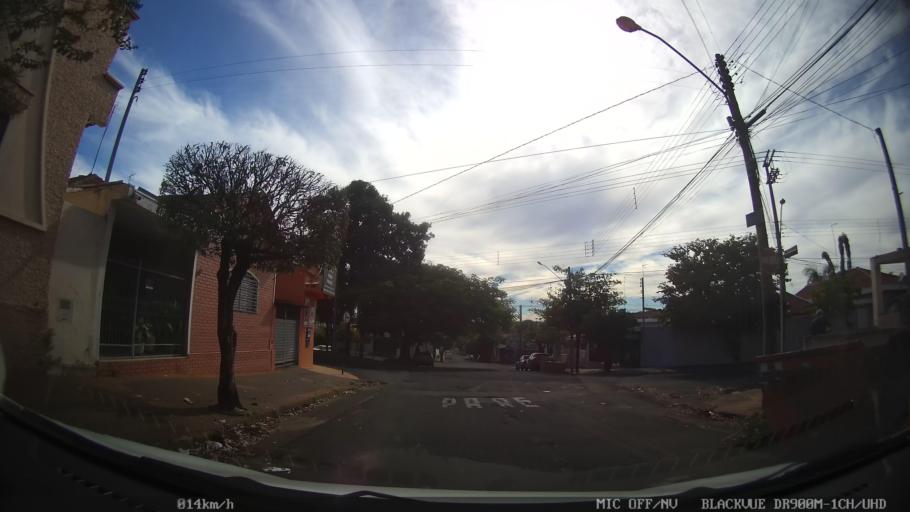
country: BR
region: Sao Paulo
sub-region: Catanduva
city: Catanduva
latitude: -21.1319
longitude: -48.9801
